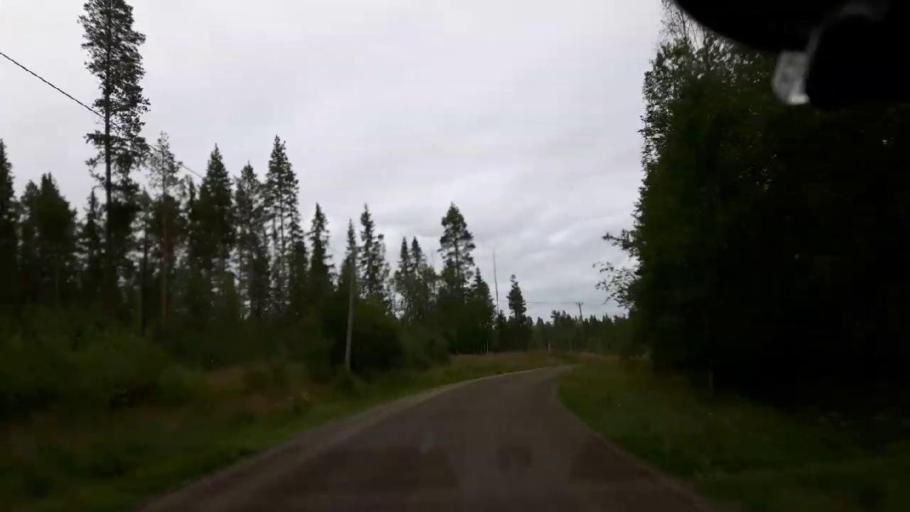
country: SE
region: Jaemtland
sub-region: Braecke Kommun
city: Braecke
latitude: 63.0288
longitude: 15.3726
